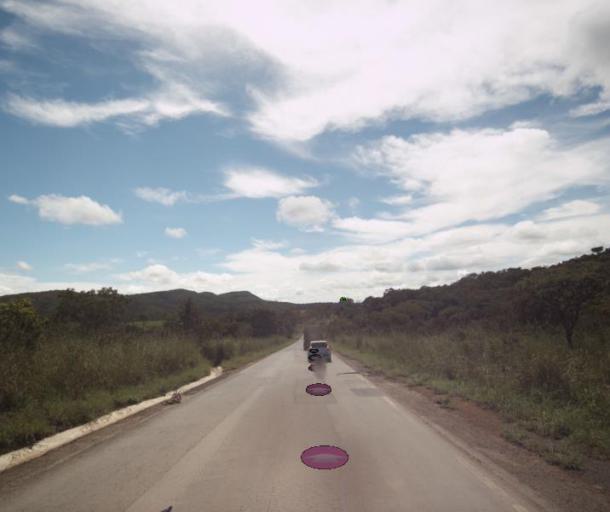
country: BR
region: Goias
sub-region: Padre Bernardo
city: Padre Bernardo
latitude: -15.4603
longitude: -48.2170
